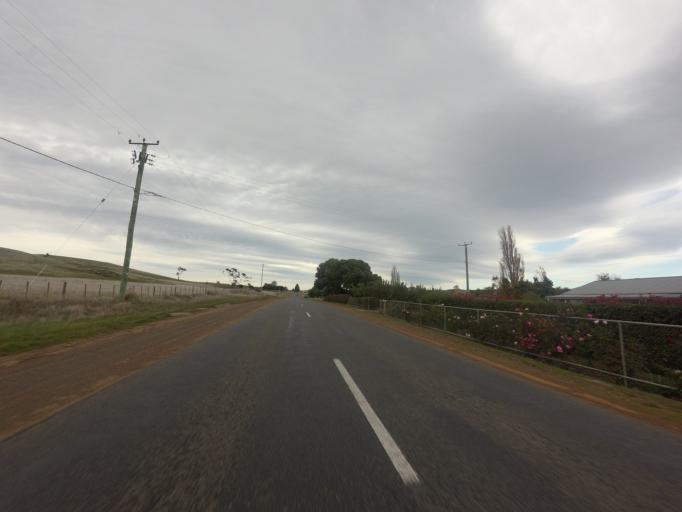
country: AU
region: Tasmania
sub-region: Derwent Valley
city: New Norfolk
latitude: -42.5091
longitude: 146.7399
